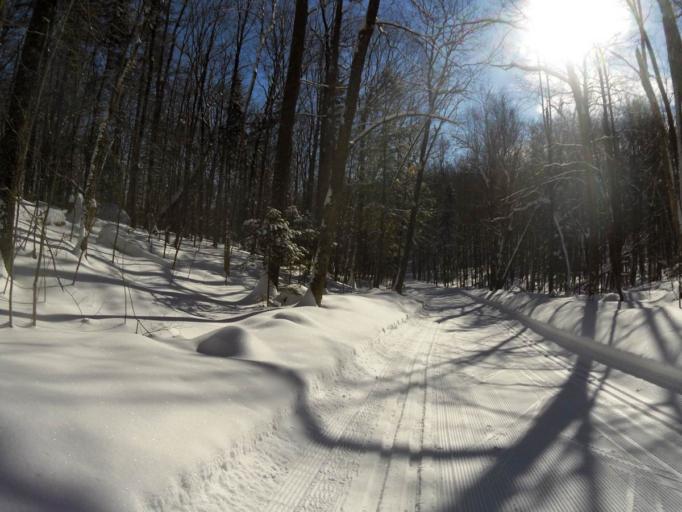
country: CA
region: Quebec
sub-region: Outaouais
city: Wakefield
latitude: 45.5830
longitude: -75.9667
